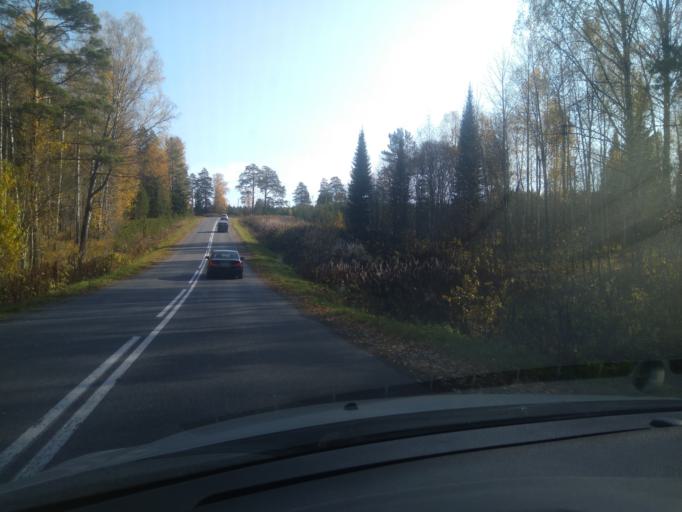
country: RU
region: Sverdlovsk
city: Mikhaylovsk
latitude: 56.5320
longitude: 59.2070
